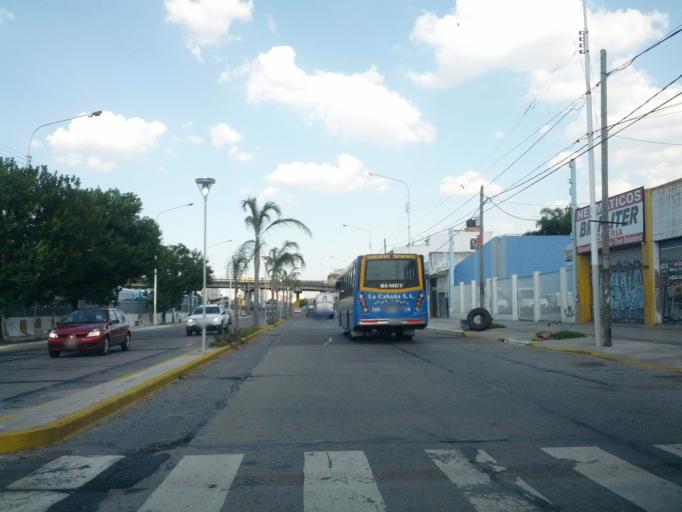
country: AR
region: Buenos Aires
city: San Justo
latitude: -34.6401
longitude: -58.5510
